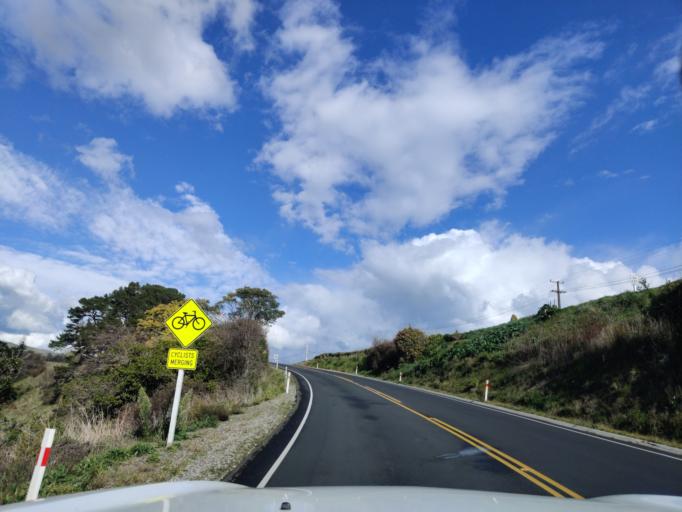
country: NZ
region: Manawatu-Wanganui
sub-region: Palmerston North City
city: Palmerston North
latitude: -40.2803
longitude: 175.7606
